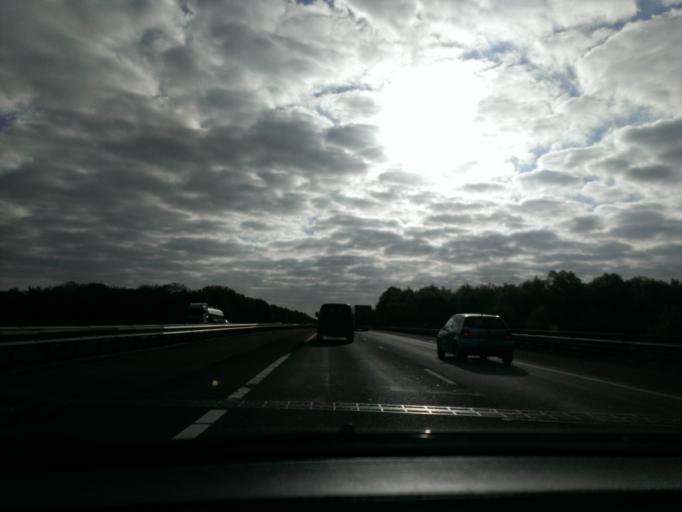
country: NL
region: Overijssel
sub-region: Gemeente Almelo
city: Almelo
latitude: 52.2926
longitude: 6.6385
